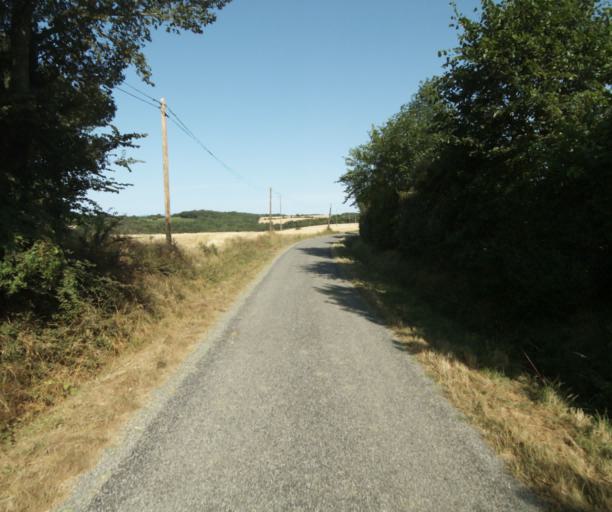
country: FR
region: Midi-Pyrenees
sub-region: Departement de la Haute-Garonne
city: Saint-Felix-Lauragais
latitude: 43.4283
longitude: 1.8257
